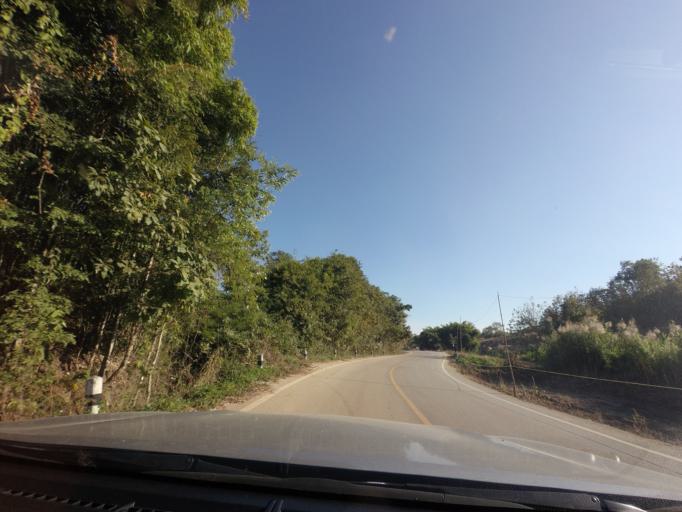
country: TH
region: Lampang
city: Chae Hom
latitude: 18.5373
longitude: 99.6419
